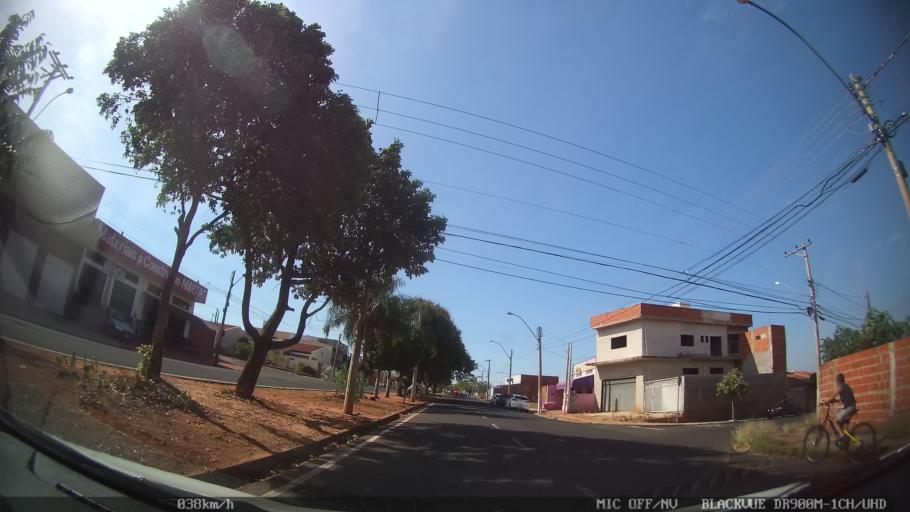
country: BR
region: Sao Paulo
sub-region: Sao Jose Do Rio Preto
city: Sao Jose do Rio Preto
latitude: -20.7917
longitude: -49.4397
